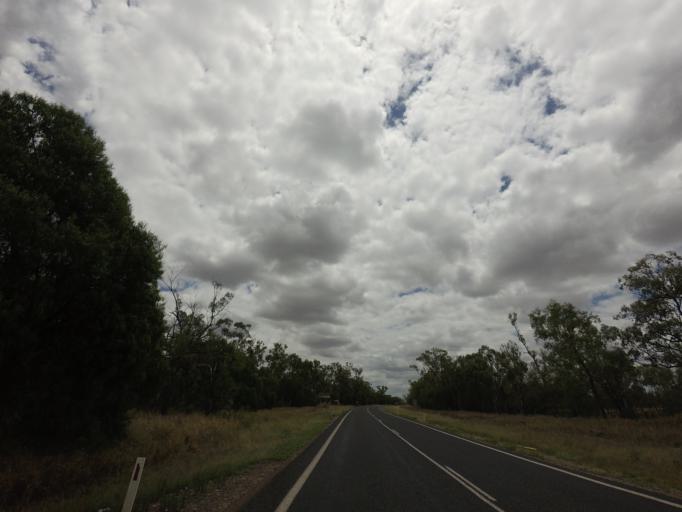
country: AU
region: Queensland
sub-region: Goondiwindi
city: Goondiwindi
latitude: -28.4930
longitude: 150.2921
